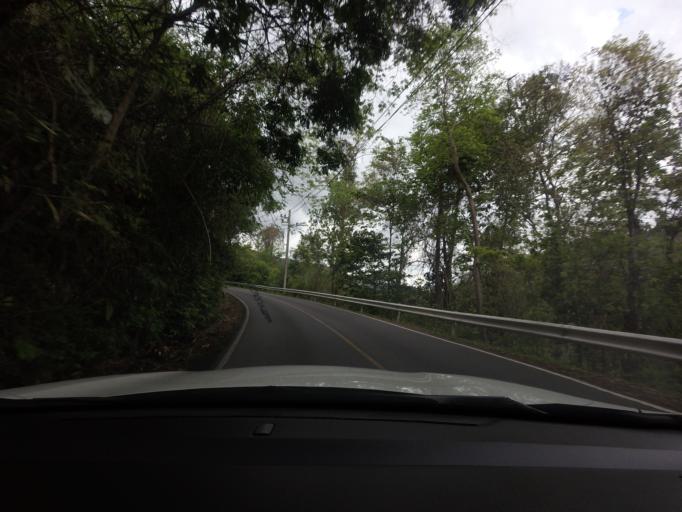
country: TH
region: Nakhon Ratchasima
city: Pak Chong
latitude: 14.4835
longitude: 101.3888
